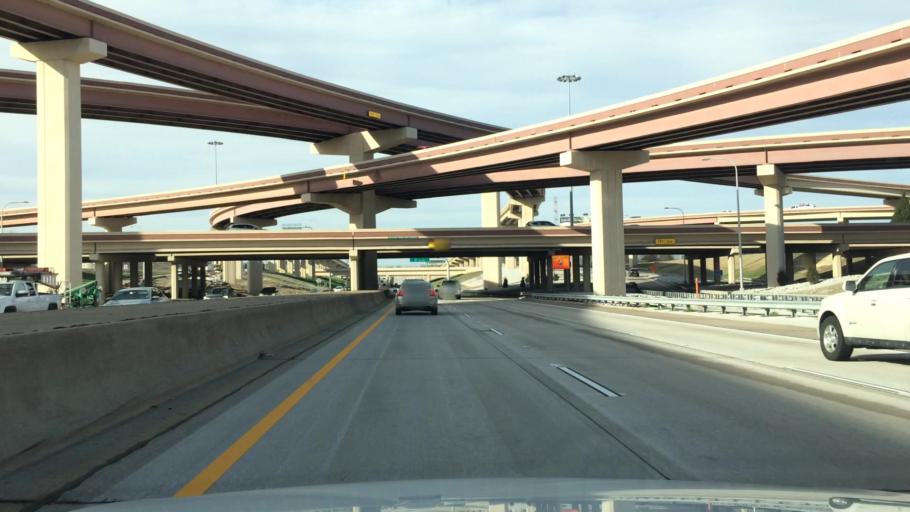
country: US
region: Texas
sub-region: Dallas County
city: Addison
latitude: 33.0118
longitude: -96.8291
